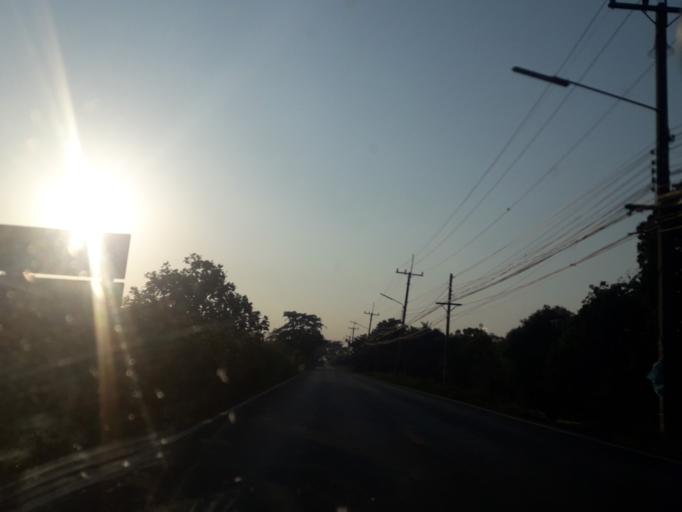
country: TH
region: Pathum Thani
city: Nong Suea
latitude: 14.1317
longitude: 100.8063
